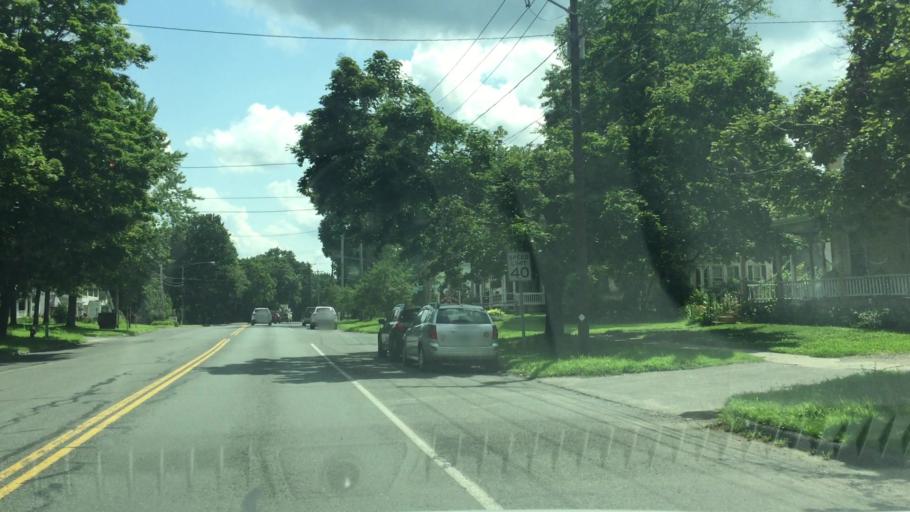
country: US
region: Massachusetts
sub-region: Berkshire County
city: Great Barrington
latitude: 42.1881
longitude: -73.3644
